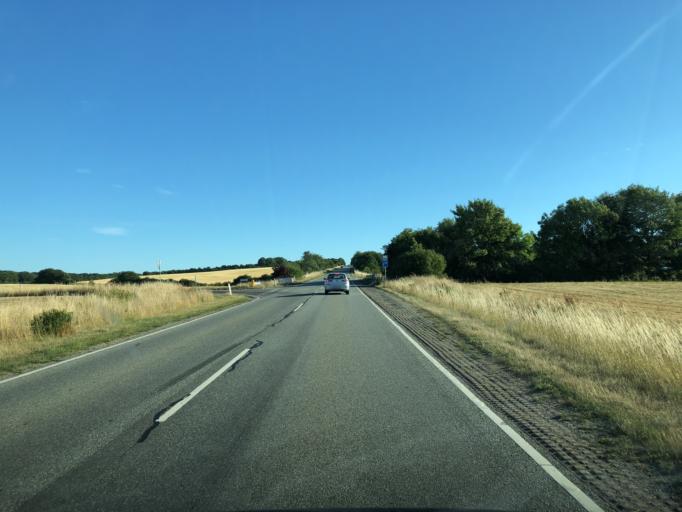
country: DK
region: Central Jutland
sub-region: Arhus Kommune
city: Framlev
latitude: 56.1260
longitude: 9.9934
